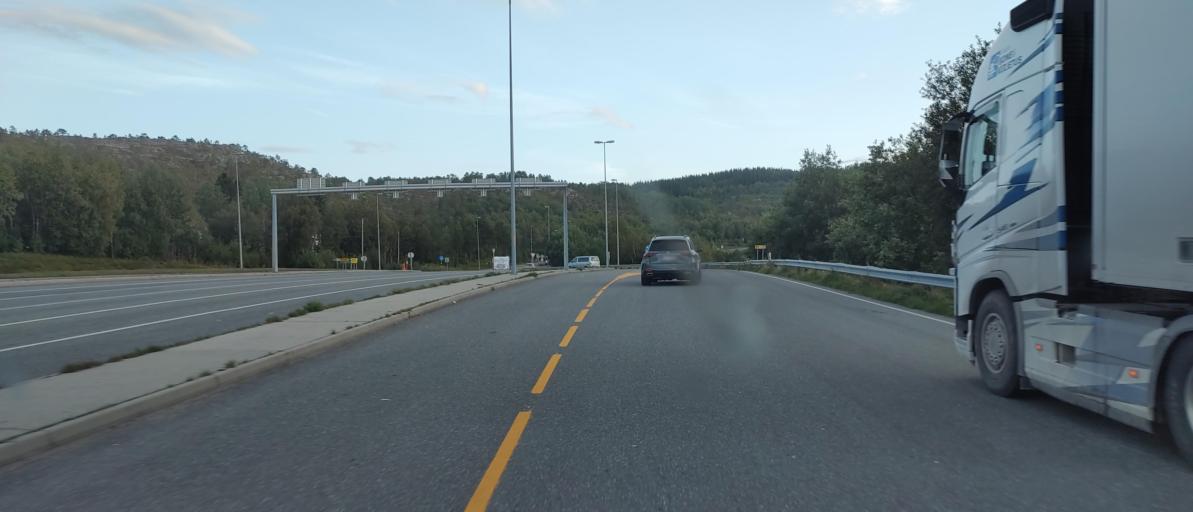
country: NO
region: Nordland
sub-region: Lodingen
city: Lodingen
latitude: 68.2227
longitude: 16.0716
